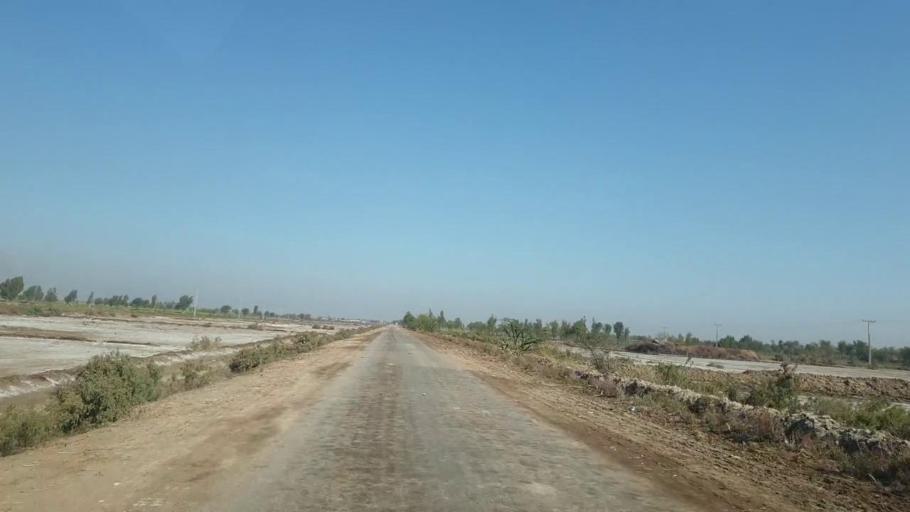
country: PK
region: Sindh
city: Mirpur Khas
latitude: 25.5838
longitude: 69.0457
